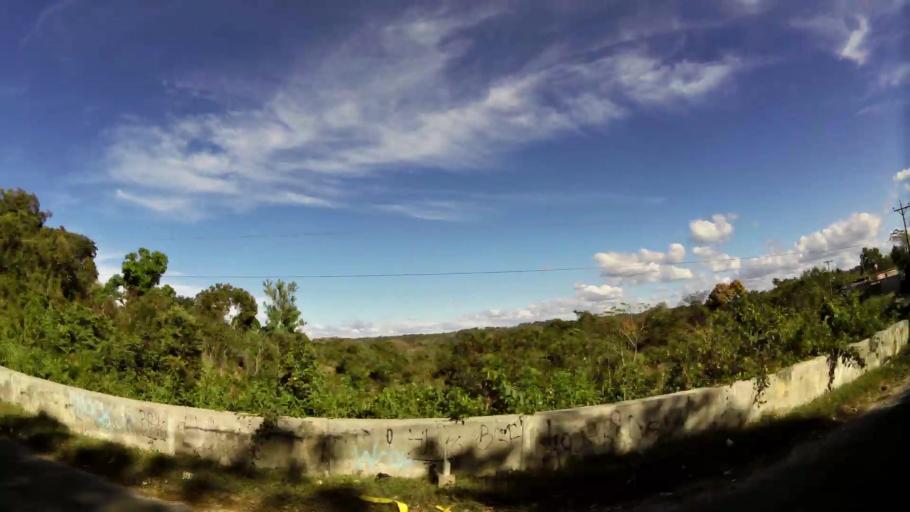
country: SV
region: Cuscatlan
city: Tenancingo
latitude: 13.8297
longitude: -89.0314
